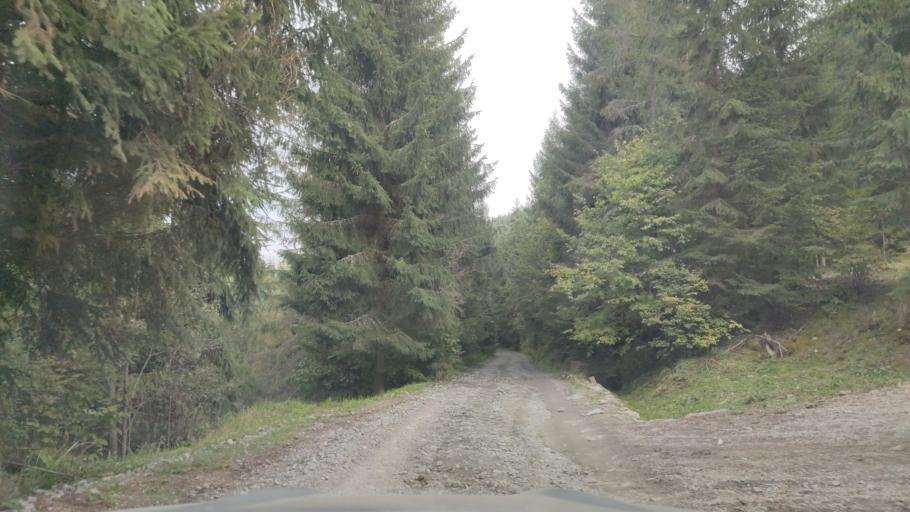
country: RO
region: Harghita
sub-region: Comuna Remetea
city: Remetea
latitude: 46.8132
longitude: 25.3590
